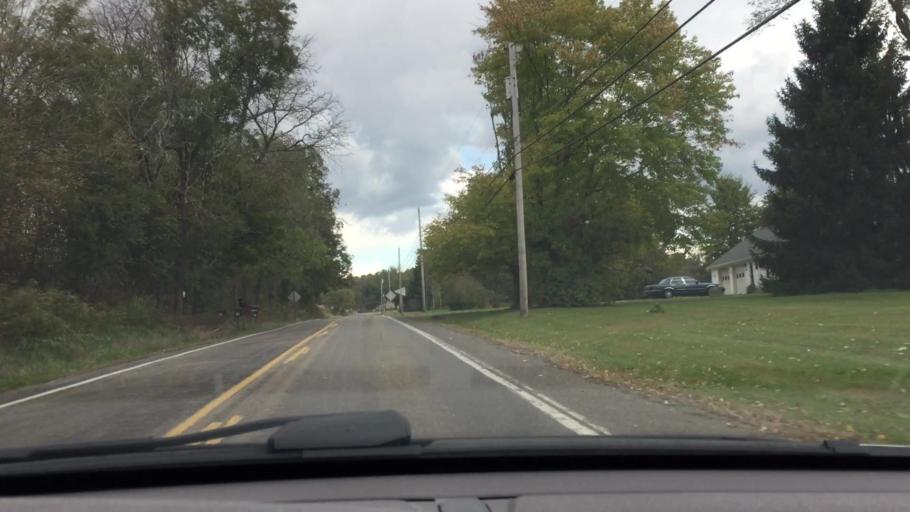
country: US
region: Pennsylvania
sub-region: Lawrence County
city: Oakwood
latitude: 41.0296
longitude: -80.4422
